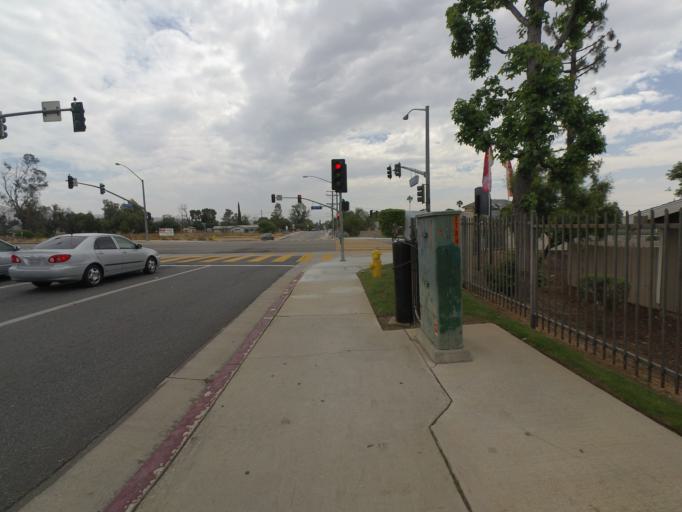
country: US
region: California
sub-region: Riverside County
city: Moreno Valley
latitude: 33.9317
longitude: -117.2442
